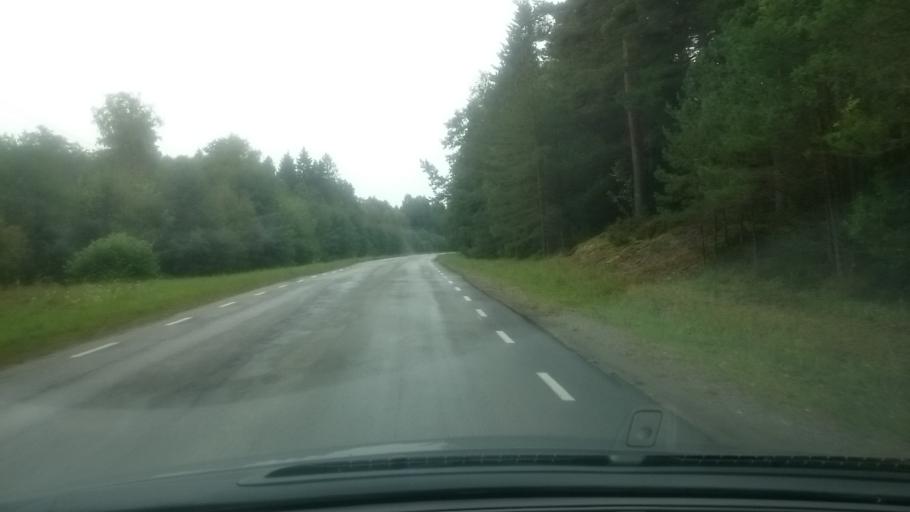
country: EE
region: Harju
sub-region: Raasiku vald
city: Raasiku
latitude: 59.4846
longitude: 25.2600
